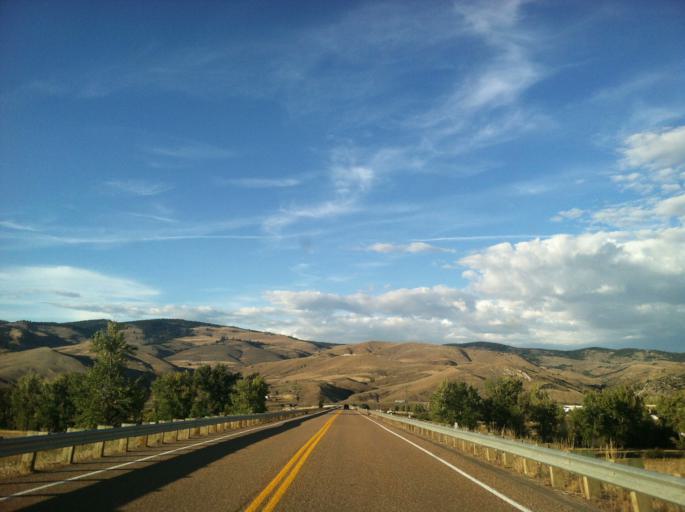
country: US
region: Montana
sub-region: Granite County
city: Philipsburg
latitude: 46.6628
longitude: -113.1566
